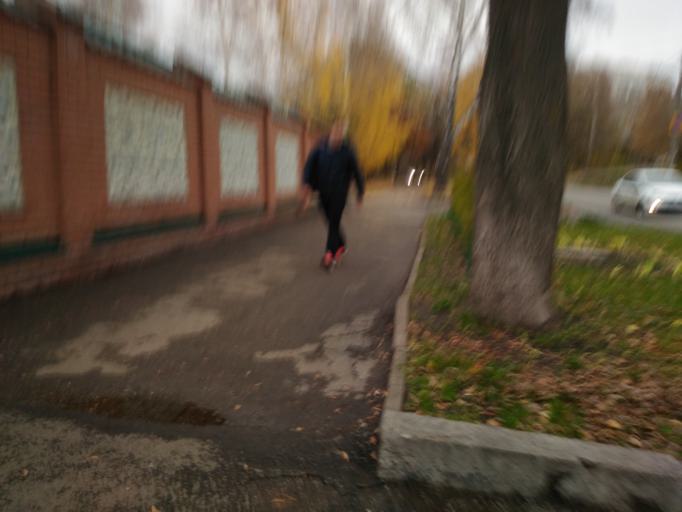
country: RU
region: Ulyanovsk
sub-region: Ulyanovskiy Rayon
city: Ulyanovsk
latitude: 54.3391
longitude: 48.3943
